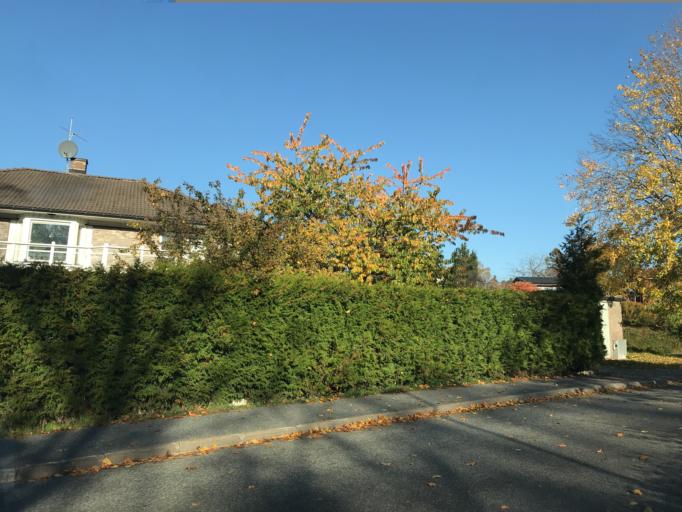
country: SE
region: Stockholm
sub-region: Sollentuna Kommun
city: Sollentuna
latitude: 59.4272
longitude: 17.9309
